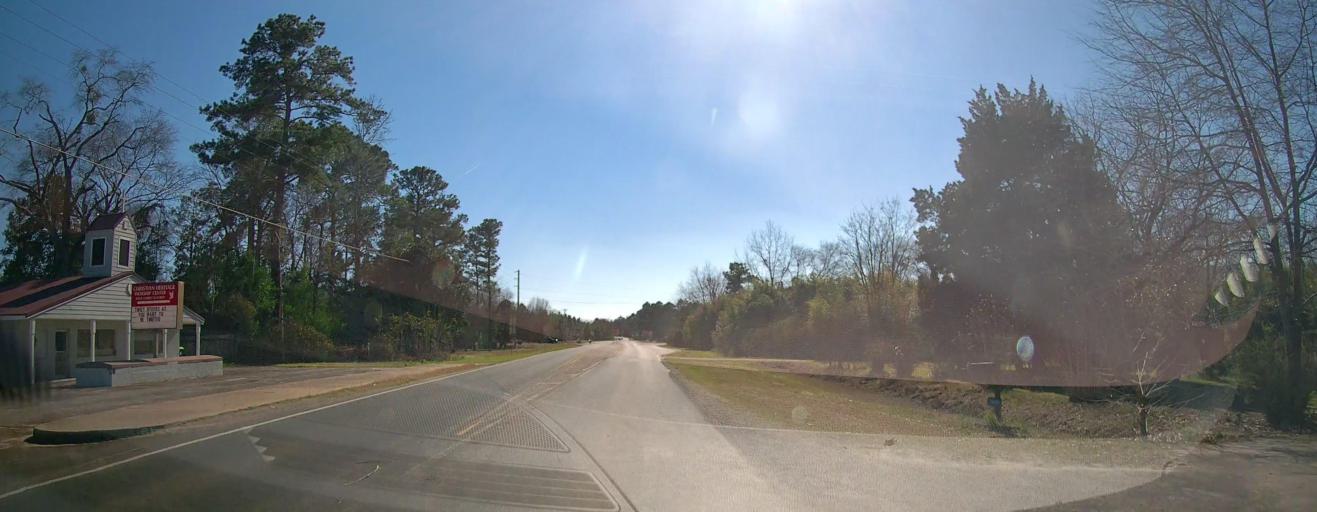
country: US
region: Georgia
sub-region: Macon County
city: Oglethorpe
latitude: 32.2710
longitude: -84.0807
